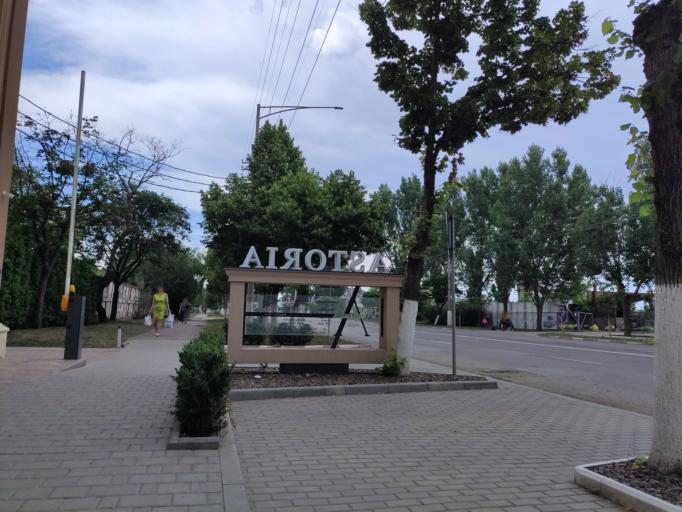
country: MD
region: Balti
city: Balti
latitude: 47.7603
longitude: 27.9408
